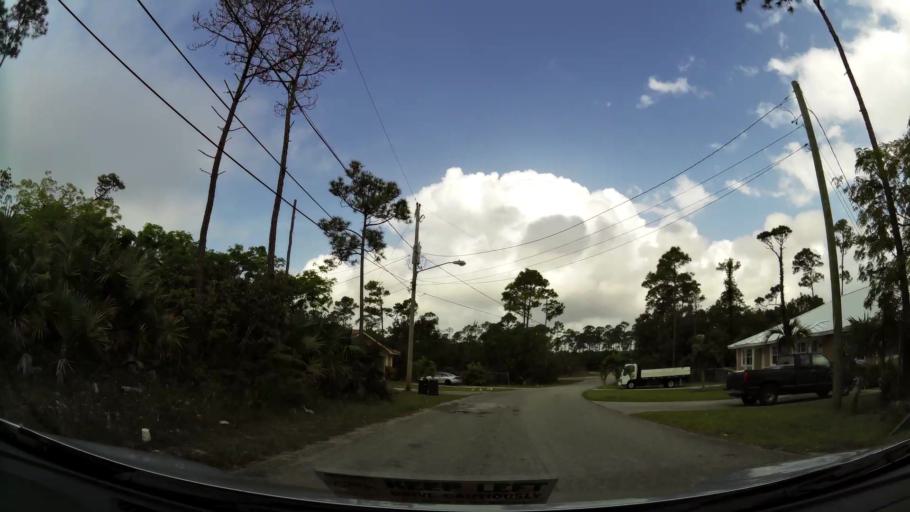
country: BS
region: Freeport
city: Lucaya
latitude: 26.5440
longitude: -78.5908
